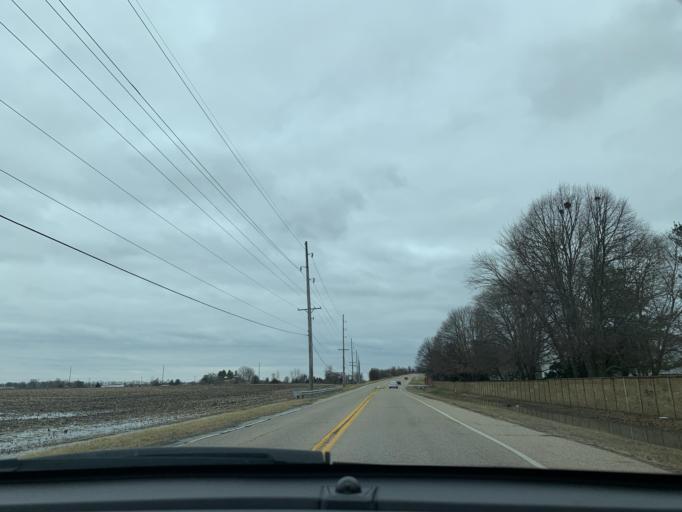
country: US
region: Illinois
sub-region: Sangamon County
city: Jerome
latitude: 39.7476
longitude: -89.6866
